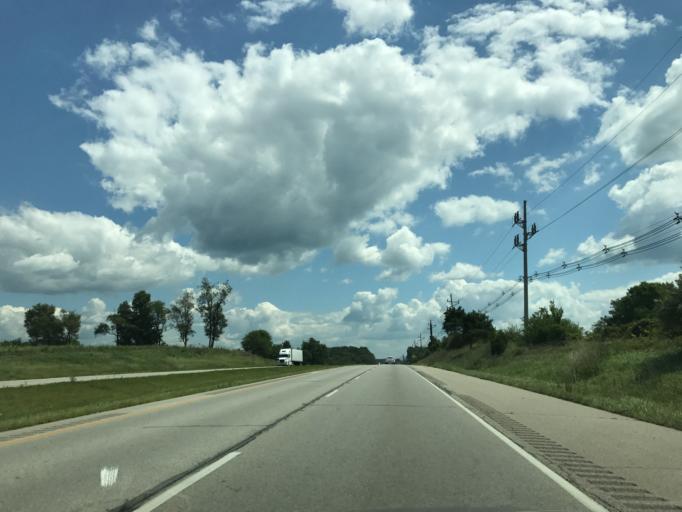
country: US
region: Indiana
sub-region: Kosciusko County
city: Pierceton
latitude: 41.2092
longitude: -85.7339
